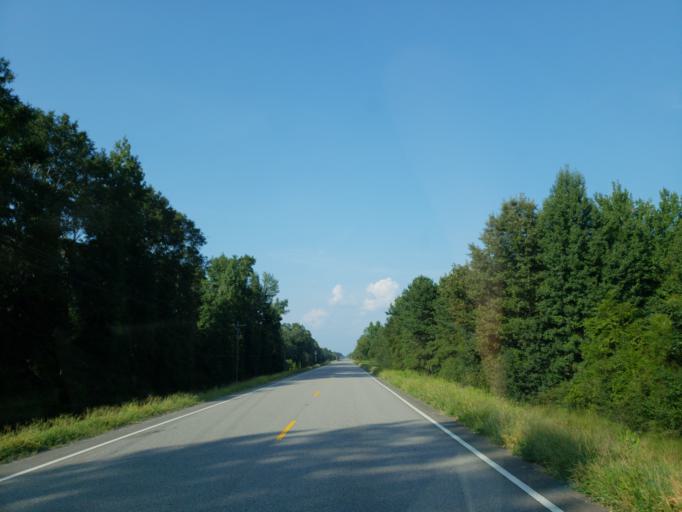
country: US
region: Alabama
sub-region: Sumter County
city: Livingston
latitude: 32.7094
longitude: -88.0819
